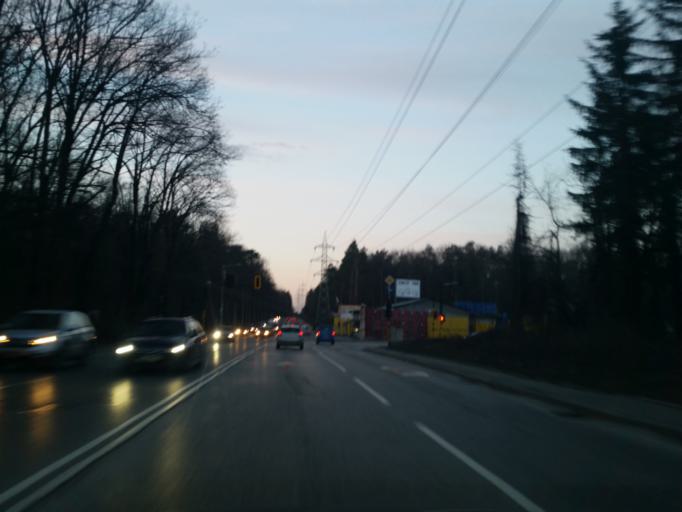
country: BG
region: Sofia-Capital
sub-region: Stolichna Obshtina
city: Sofia
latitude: 42.6660
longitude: 23.3375
